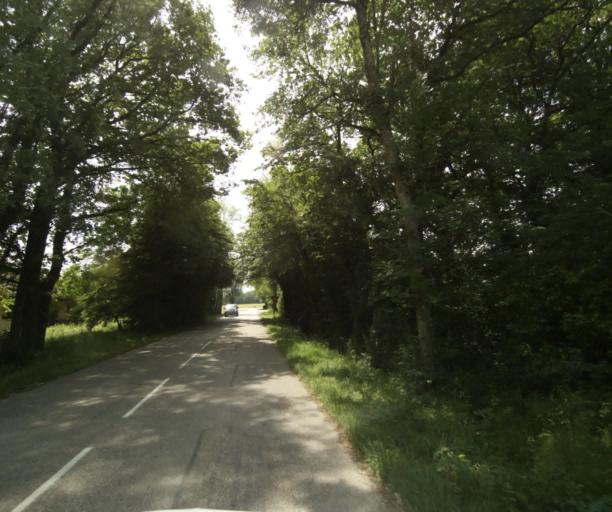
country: FR
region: Rhone-Alpes
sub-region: Departement de la Haute-Savoie
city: Perrignier
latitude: 46.3023
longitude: 6.4173
